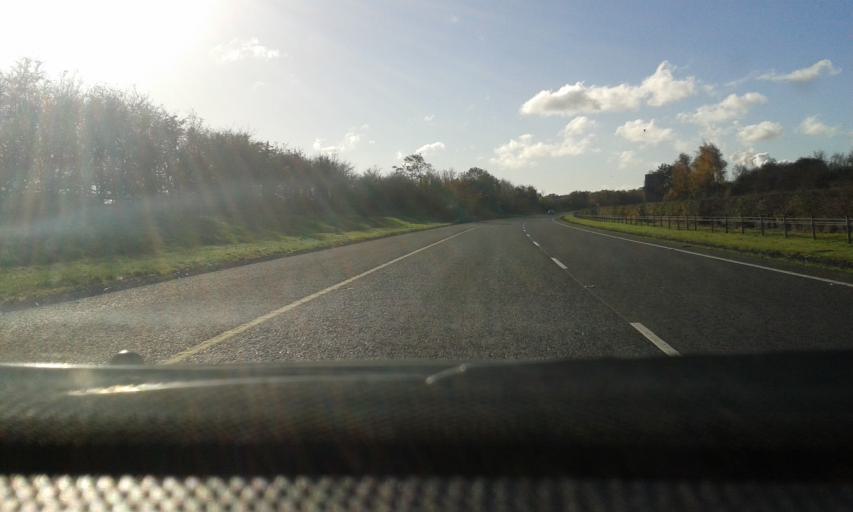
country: IE
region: Leinster
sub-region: Laois
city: Portlaoise
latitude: 53.0384
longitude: -7.2443
